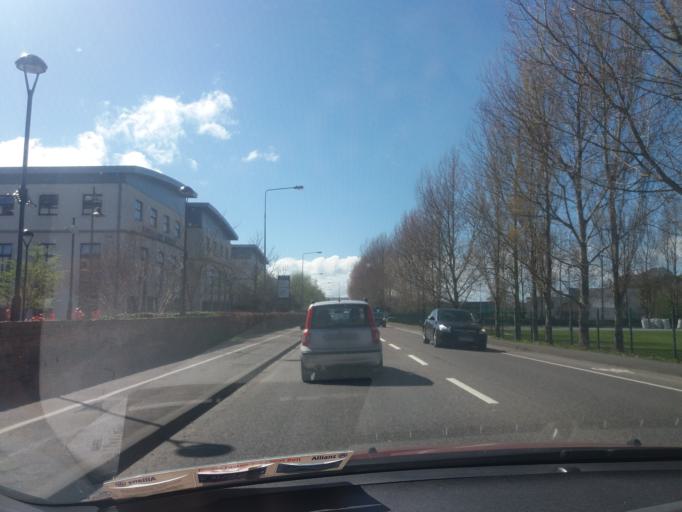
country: IE
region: Munster
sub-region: Ciarrai
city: Tralee
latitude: 52.2639
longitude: -9.7012
